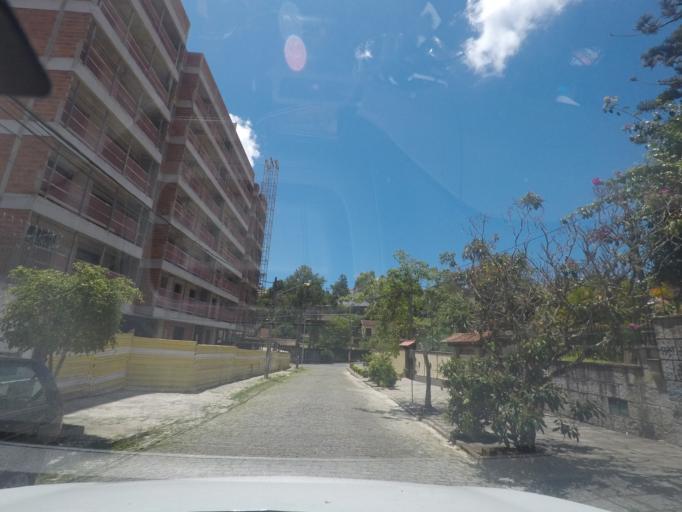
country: BR
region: Rio de Janeiro
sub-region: Teresopolis
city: Teresopolis
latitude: -22.4305
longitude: -42.9821
